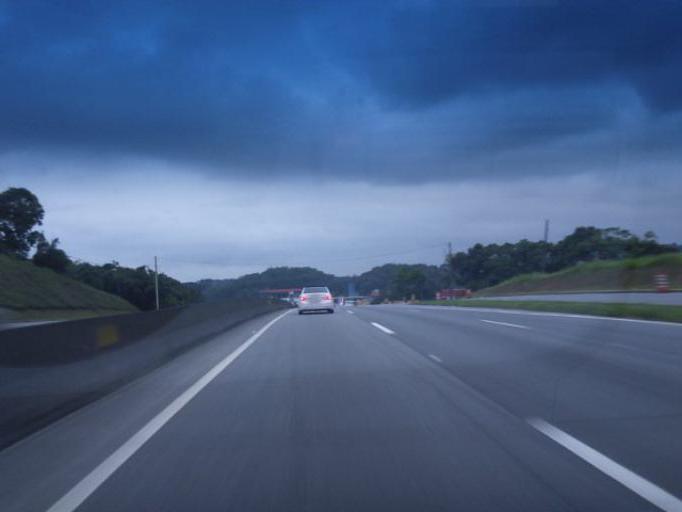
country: BR
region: Santa Catarina
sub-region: Joinville
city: Joinville
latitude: -26.3521
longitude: -48.8583
